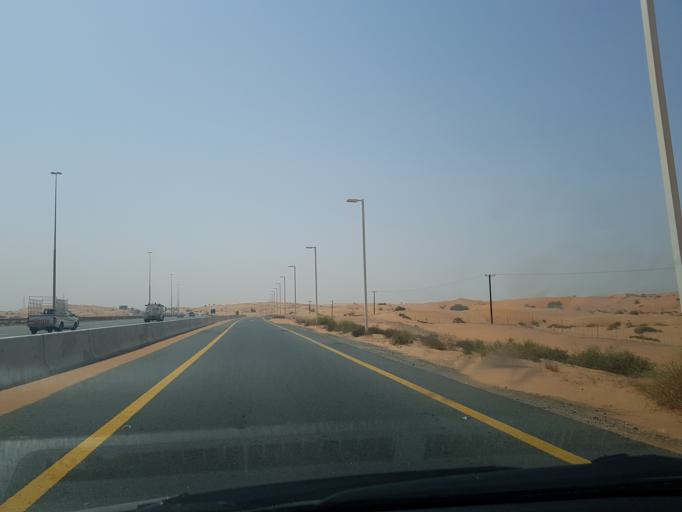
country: AE
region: Ra's al Khaymah
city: Ras al-Khaimah
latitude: 25.6232
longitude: 55.8055
